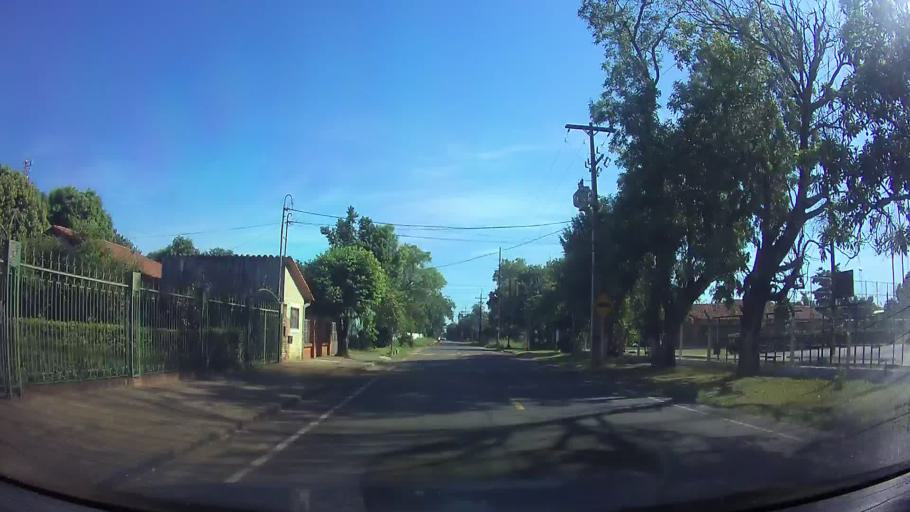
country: PY
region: Central
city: San Lorenzo
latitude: -25.2769
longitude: -57.5052
